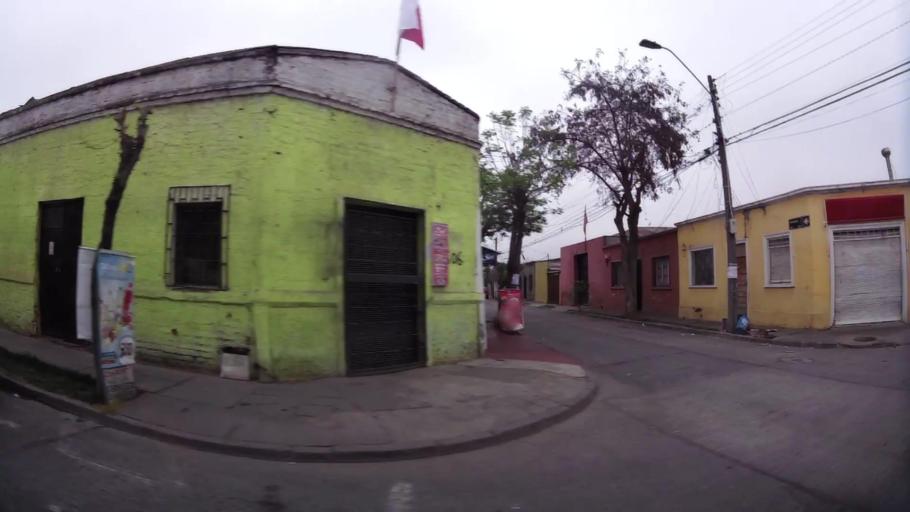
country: CL
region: Santiago Metropolitan
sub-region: Provincia de Santiago
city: Santiago
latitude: -33.4968
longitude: -70.6419
